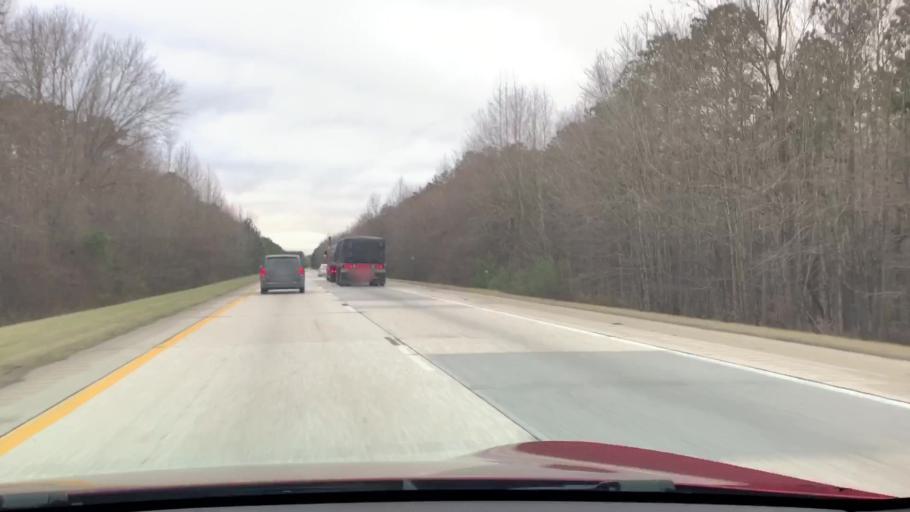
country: US
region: South Carolina
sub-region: Dillon County
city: Latta
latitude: 34.3224
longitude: -79.5839
